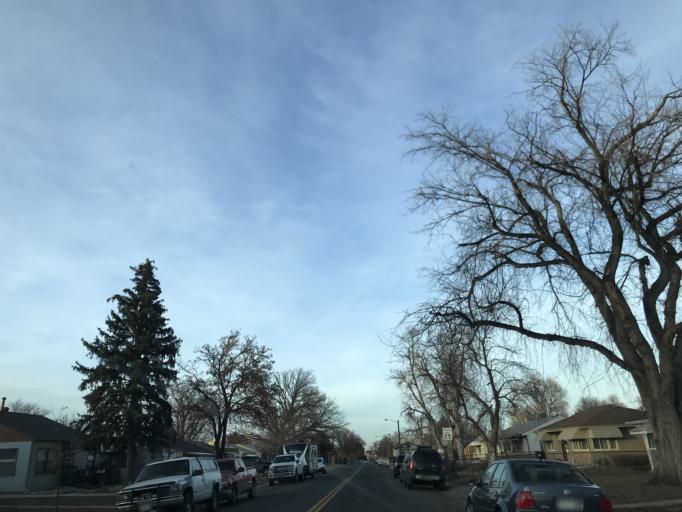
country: US
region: Colorado
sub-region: Adams County
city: Aurora
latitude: 39.7477
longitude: -104.8658
